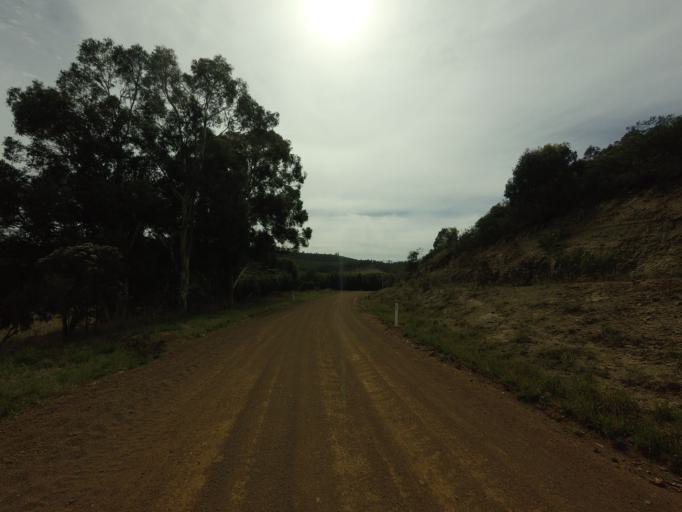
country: AU
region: Tasmania
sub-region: Sorell
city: Sorell
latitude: -42.4773
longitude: 147.5902
